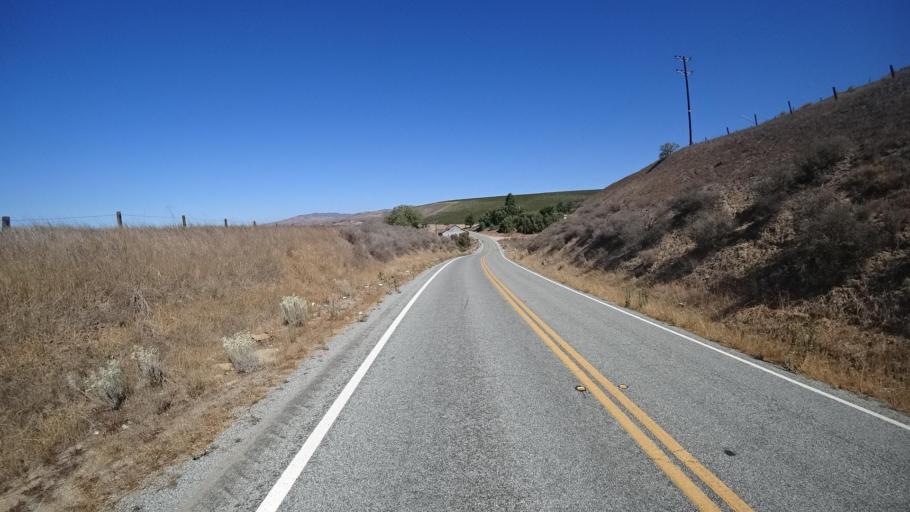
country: US
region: California
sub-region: Monterey County
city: Greenfield
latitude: 36.3897
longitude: -121.2486
